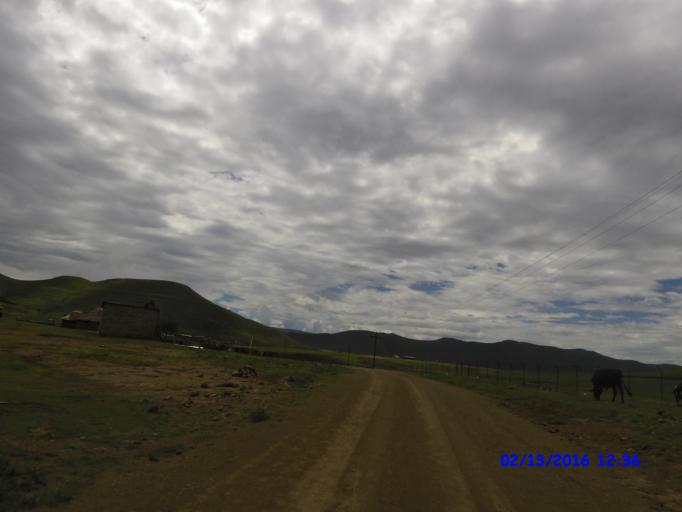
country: LS
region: Maseru
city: Nako
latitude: -29.8406
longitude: 28.0240
